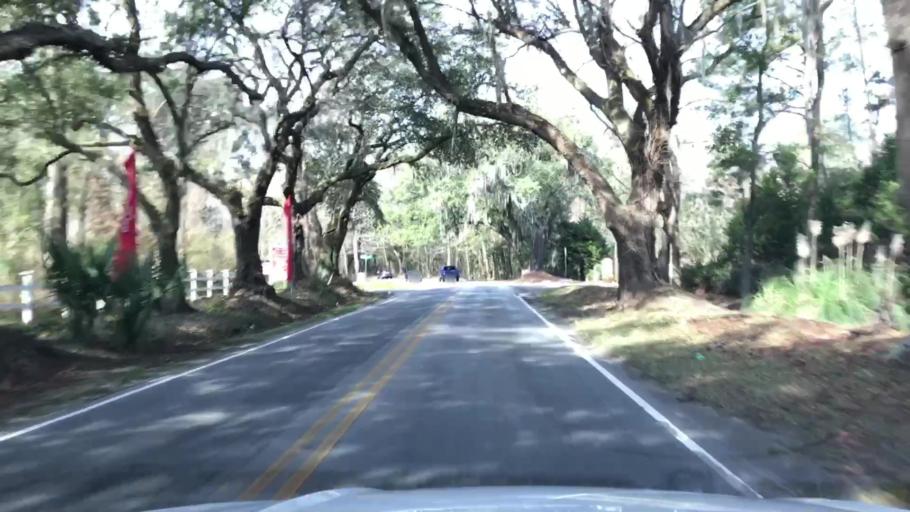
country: US
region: South Carolina
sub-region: Charleston County
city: Shell Point
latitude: 32.7518
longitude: -80.0446
